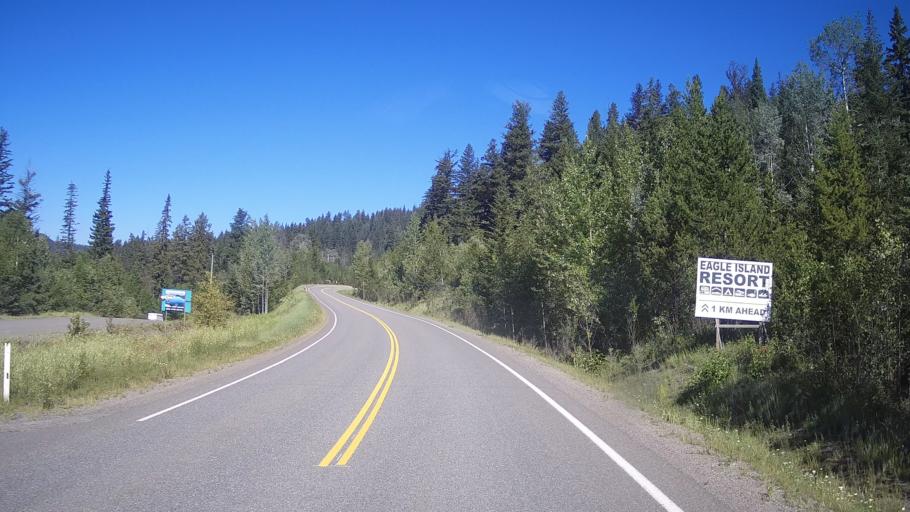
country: CA
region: British Columbia
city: Kamloops
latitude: 51.4704
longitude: -120.5348
